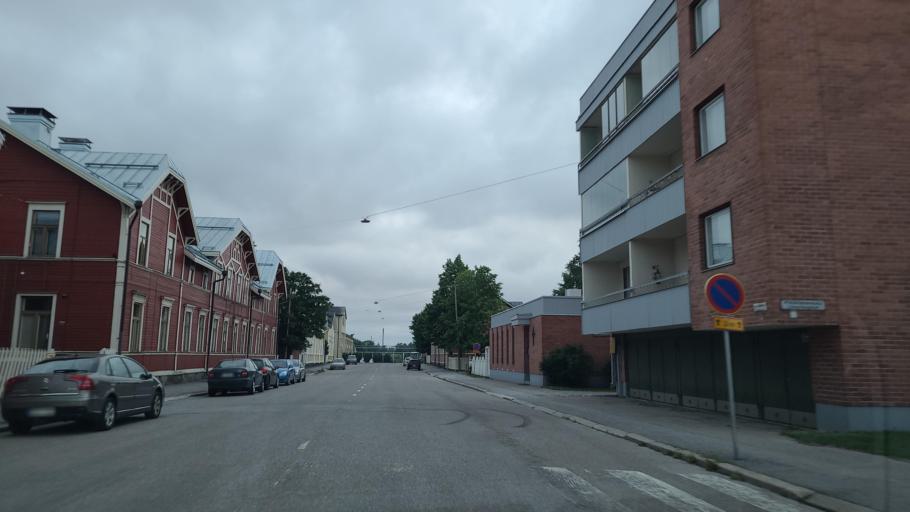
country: FI
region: Ostrobothnia
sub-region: Vaasa
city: Vaasa
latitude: 63.1033
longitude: 21.6158
